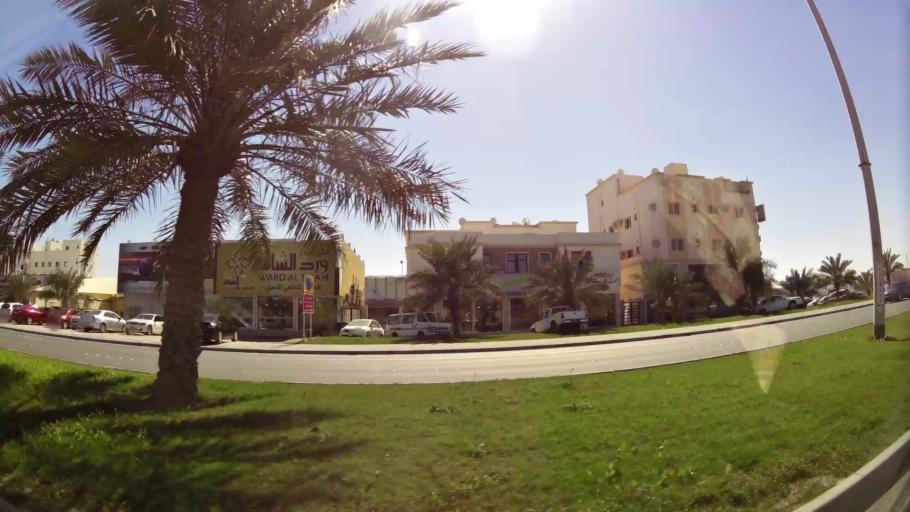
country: BH
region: Muharraq
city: Al Hadd
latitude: 26.2607
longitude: 50.6433
